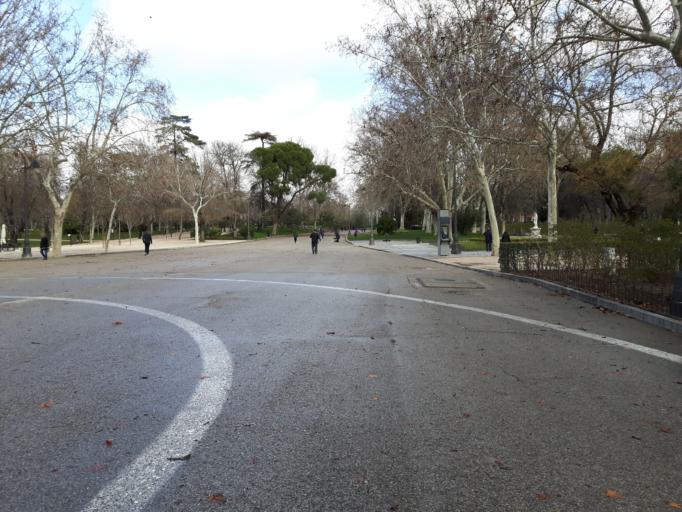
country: ES
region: Madrid
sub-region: Provincia de Madrid
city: Retiro
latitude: 40.4160
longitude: -3.6799
